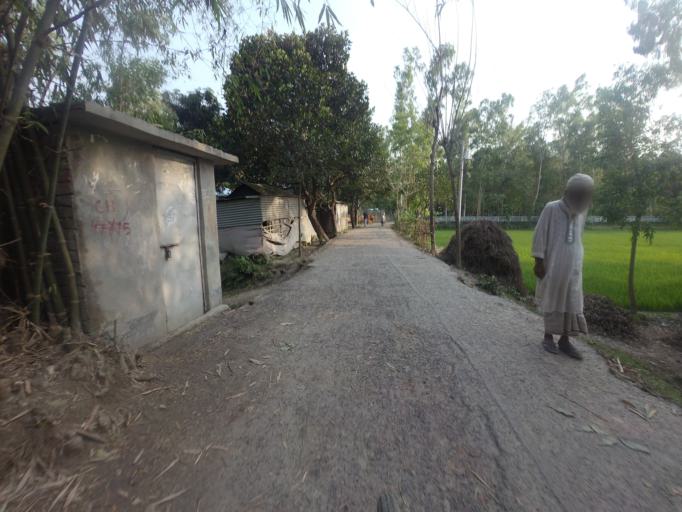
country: BD
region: Rajshahi
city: Sirajganj
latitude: 24.3301
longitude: 89.7148
